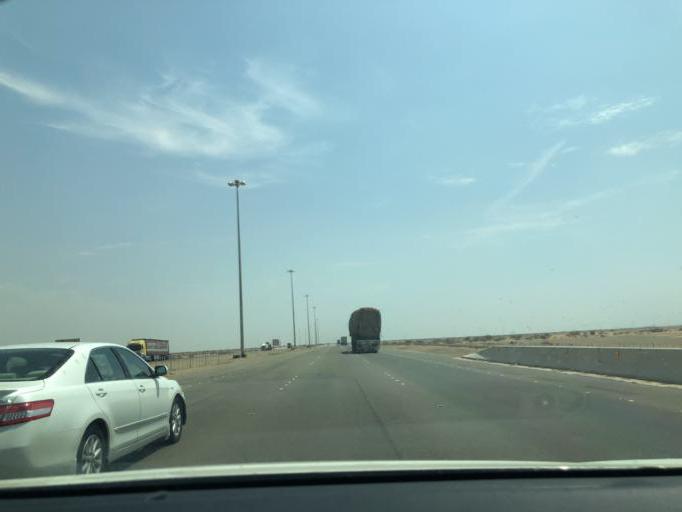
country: SA
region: Makkah
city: Rabigh
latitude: 22.2567
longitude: 39.1181
